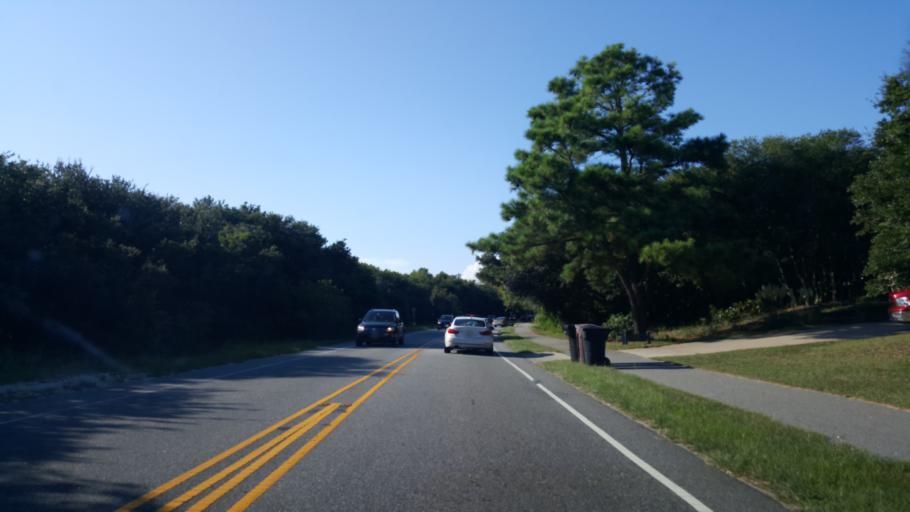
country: US
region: North Carolina
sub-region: Dare County
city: Southern Shores
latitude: 36.1455
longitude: -75.7407
